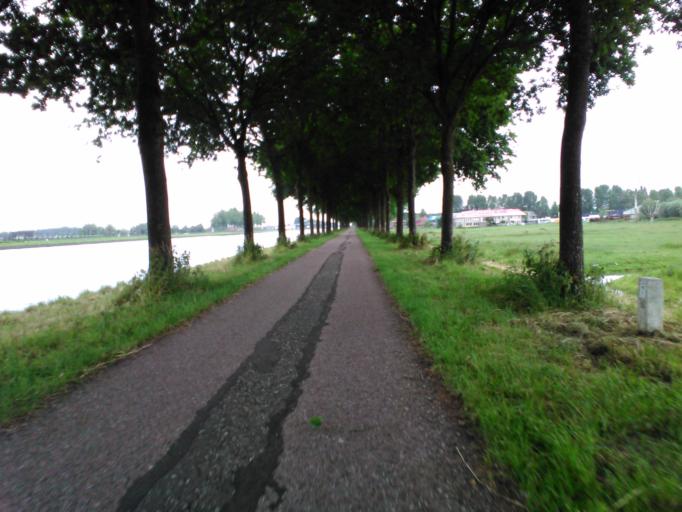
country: NL
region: Utrecht
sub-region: Stichtse Vecht
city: Vreeland
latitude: 52.2183
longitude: 5.0053
